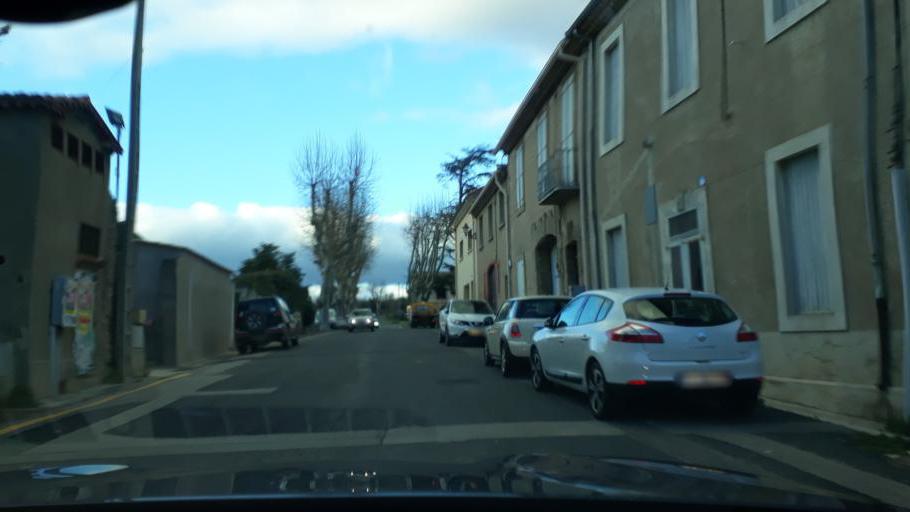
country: FR
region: Languedoc-Roussillon
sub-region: Departement de l'Herault
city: Nissan-lez-Enserune
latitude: 43.2918
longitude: 3.1278
